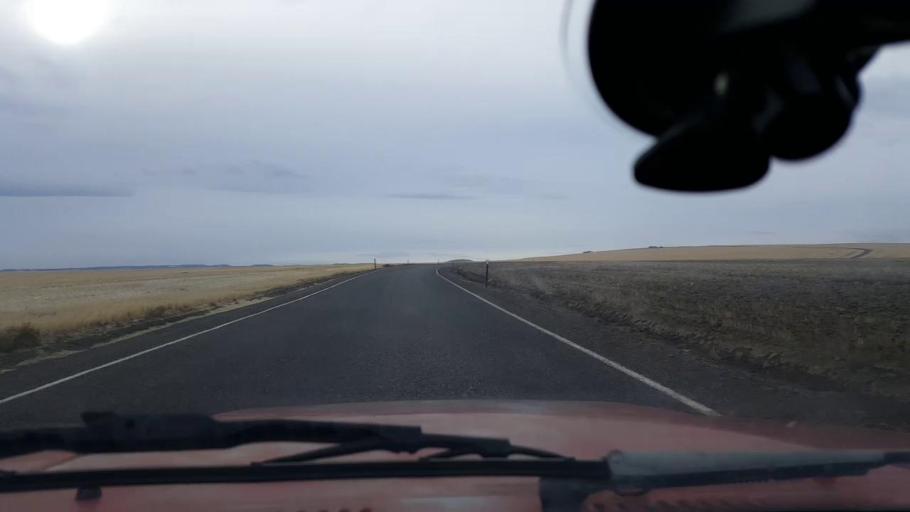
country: US
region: Washington
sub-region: Asotin County
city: Clarkston Heights-Vineland
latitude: 46.3464
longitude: -117.2398
